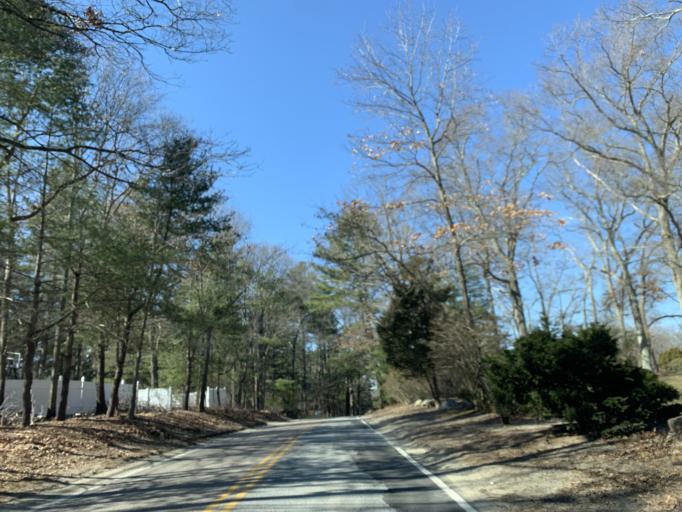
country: US
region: Massachusetts
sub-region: Norfolk County
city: Sharon
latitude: 42.1443
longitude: -71.1757
